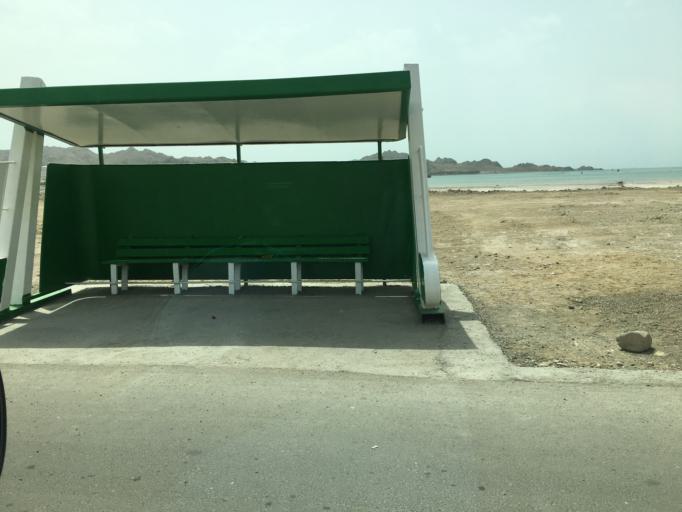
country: TM
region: Balkan
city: Turkmenbasy
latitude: 40.0066
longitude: 53.0659
